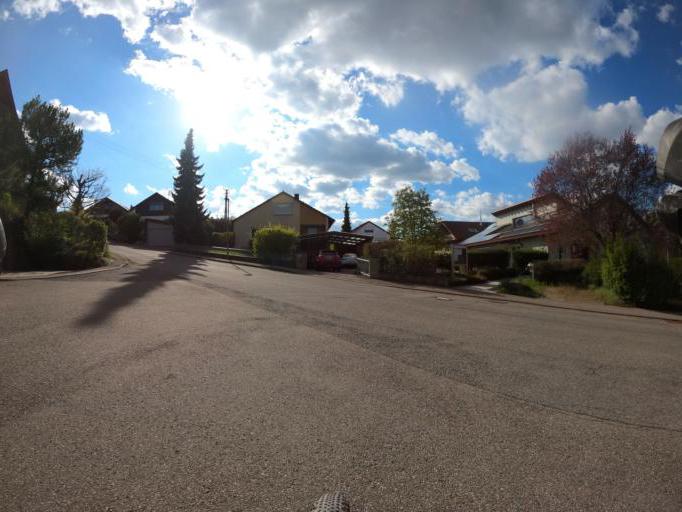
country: DE
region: Baden-Wuerttemberg
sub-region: Karlsruhe Region
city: Ostelsheim
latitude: 48.7261
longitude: 8.8452
